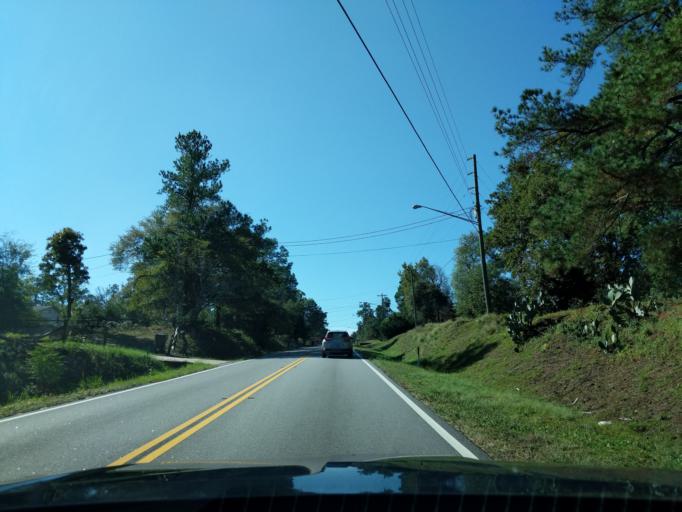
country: US
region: Georgia
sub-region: Richmond County
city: Hephzibah
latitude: 33.3322
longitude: -82.0084
